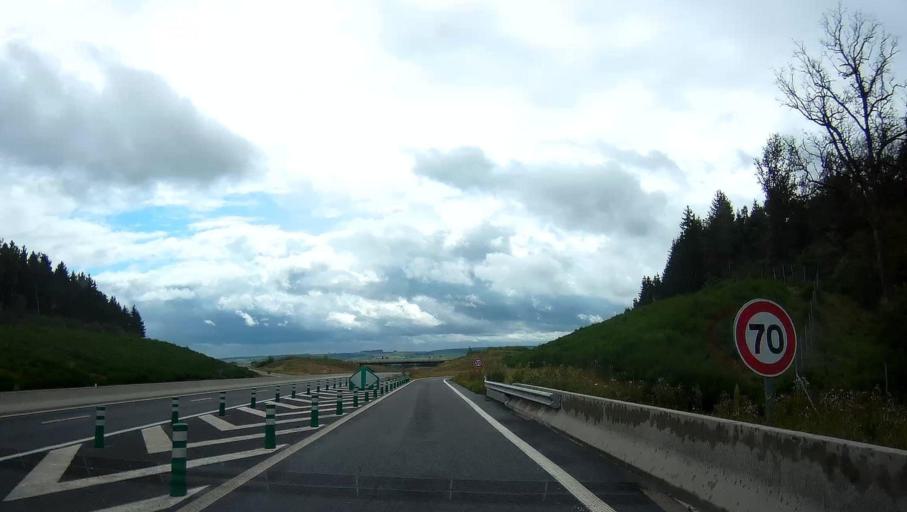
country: FR
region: Champagne-Ardenne
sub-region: Departement des Ardennes
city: Rimogne
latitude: 49.8481
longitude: 4.5135
